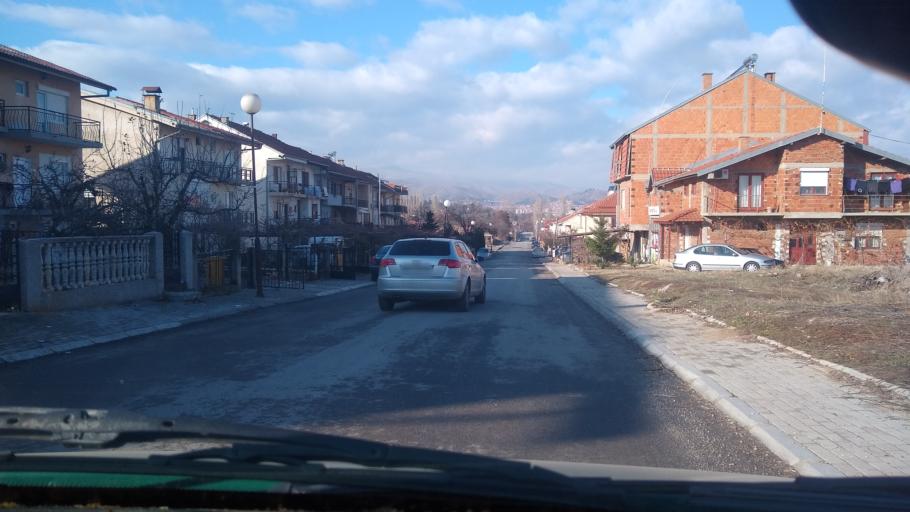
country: MK
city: Bistrica
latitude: 41.0058
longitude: 21.3490
